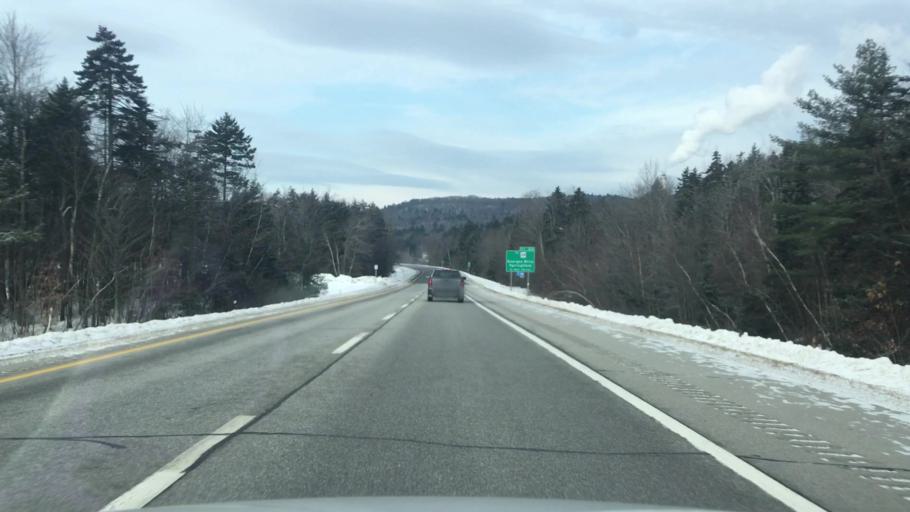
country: US
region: New Hampshire
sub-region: Sullivan County
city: Springfield
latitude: 43.4385
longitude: -72.0499
